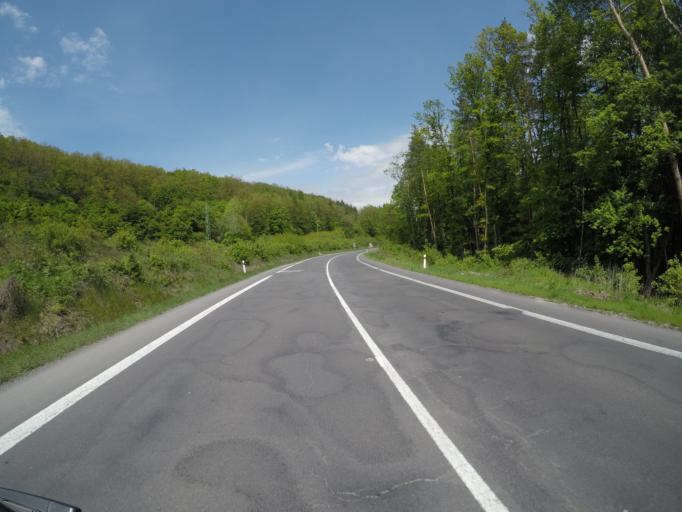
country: SK
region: Banskobystricky
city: Krupina
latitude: 48.3902
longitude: 19.0844
